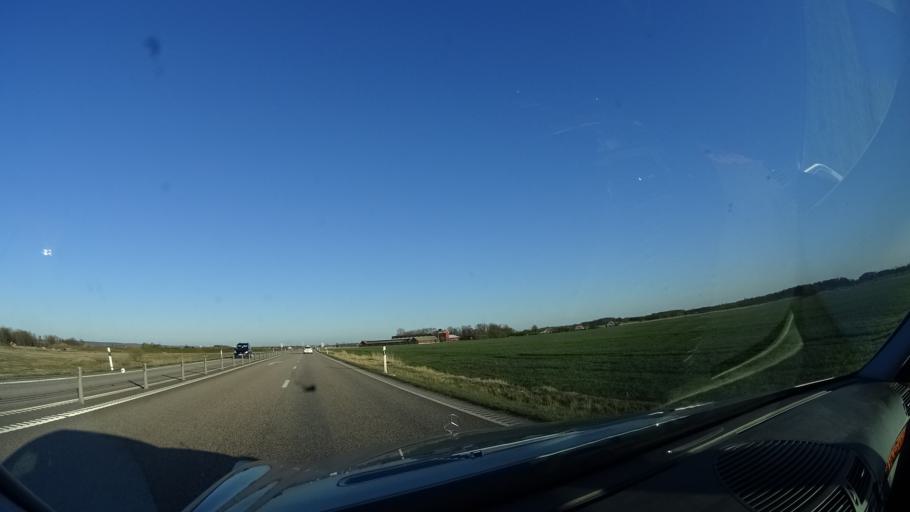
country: SE
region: Skane
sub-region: Helsingborg
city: Hyllinge
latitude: 56.0950
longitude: 12.8608
